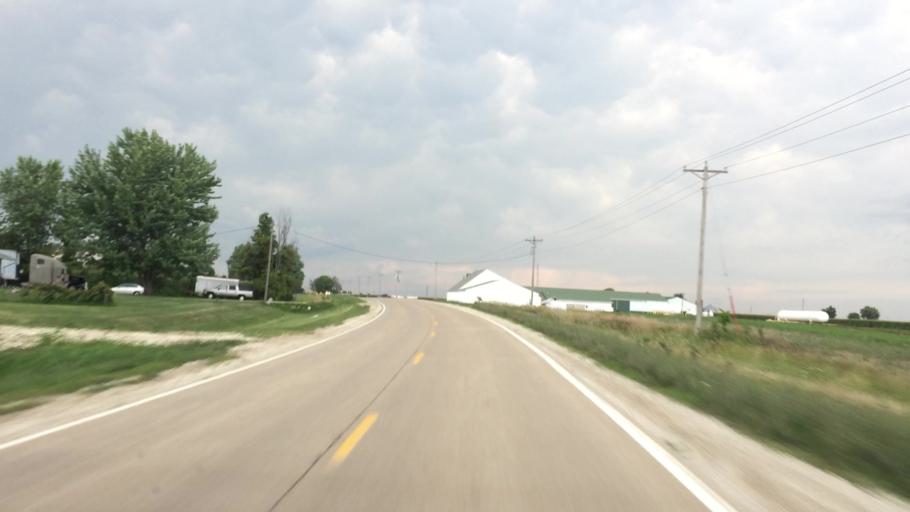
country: US
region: Iowa
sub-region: Lee County
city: Fort Madison
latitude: 40.7354
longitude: -91.3285
